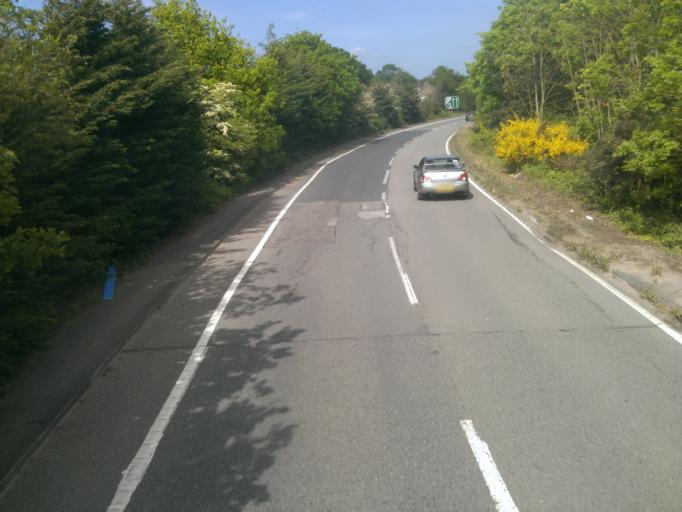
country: GB
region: England
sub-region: Essex
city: Colchester
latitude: 51.9252
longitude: 0.9362
